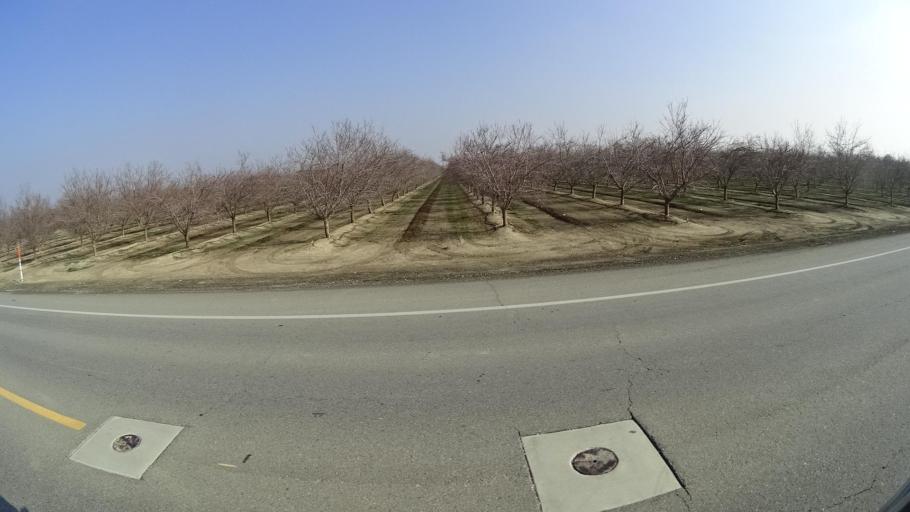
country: US
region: California
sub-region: Kern County
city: Greenfield
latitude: 35.2162
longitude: -119.1100
